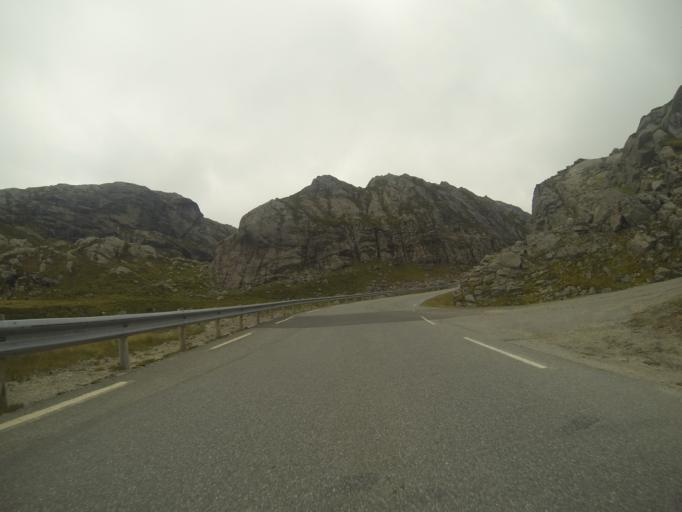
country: NO
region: Vest-Agder
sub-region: Sirdal
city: Tonstad
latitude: 59.0320
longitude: 6.6556
